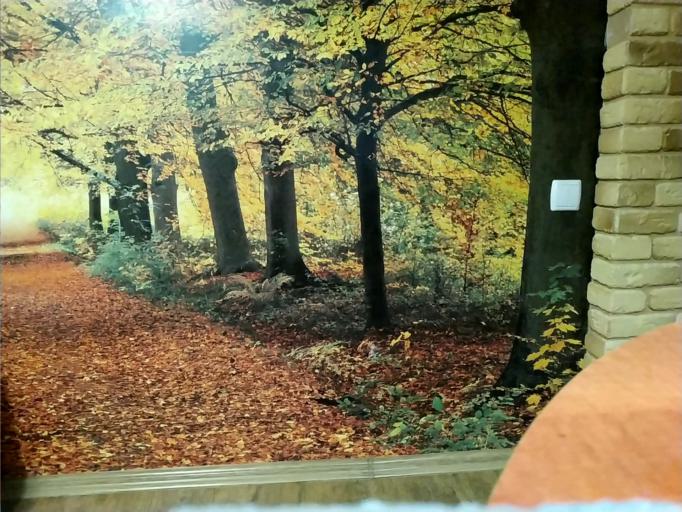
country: BY
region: Minsk
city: Plyeshchanitsy
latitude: 54.4276
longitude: 27.6123
